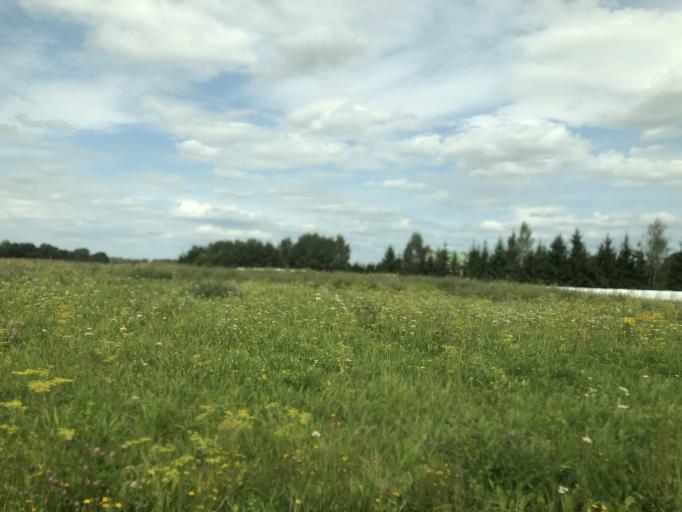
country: LV
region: Vecumnieki
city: Vecumnieki
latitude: 56.4594
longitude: 24.6122
